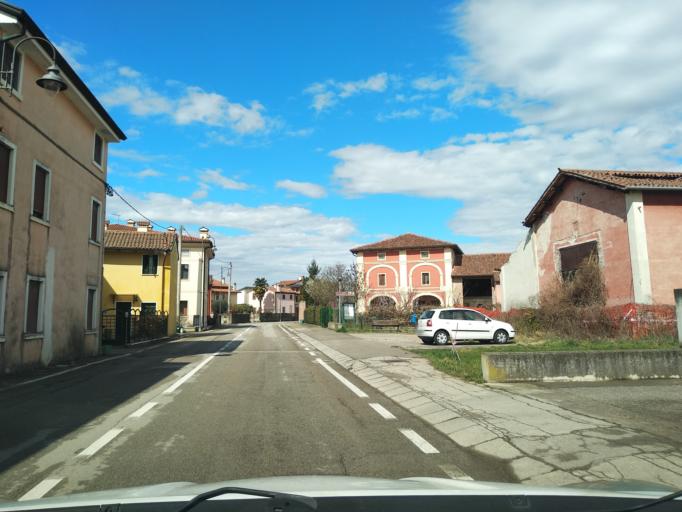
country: IT
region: Veneto
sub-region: Provincia di Vicenza
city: Bolzano Vicentino
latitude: 45.6029
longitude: 11.6134
